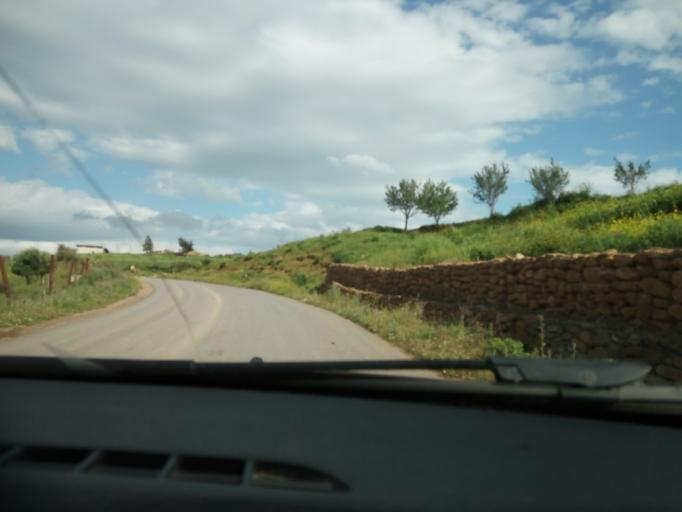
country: DZ
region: Tipaza
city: Hadjout
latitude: 36.3726
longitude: 2.4845
